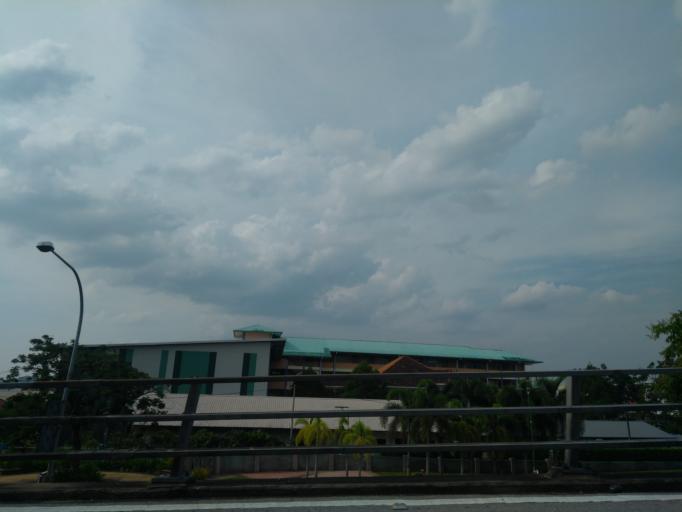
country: MY
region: Sarawak
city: Kuching
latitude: 1.5539
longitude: 110.3372
